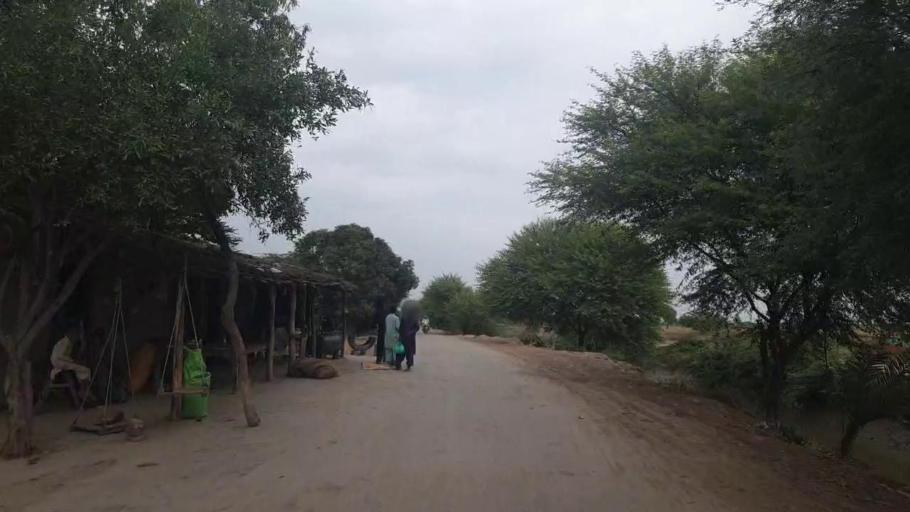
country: PK
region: Sindh
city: Badin
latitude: 24.6168
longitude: 68.6806
